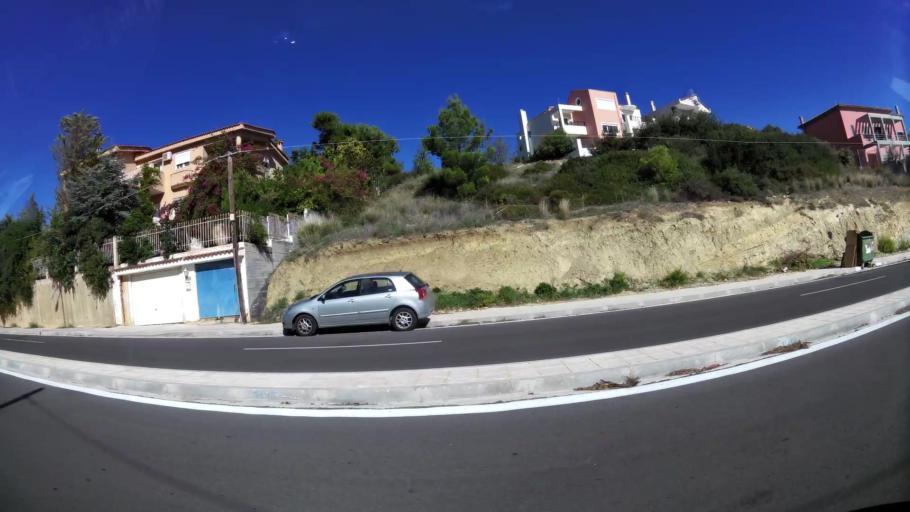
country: GR
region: Attica
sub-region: Nomarchia Anatolikis Attikis
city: Dhrafi
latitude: 38.0066
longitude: 23.9131
